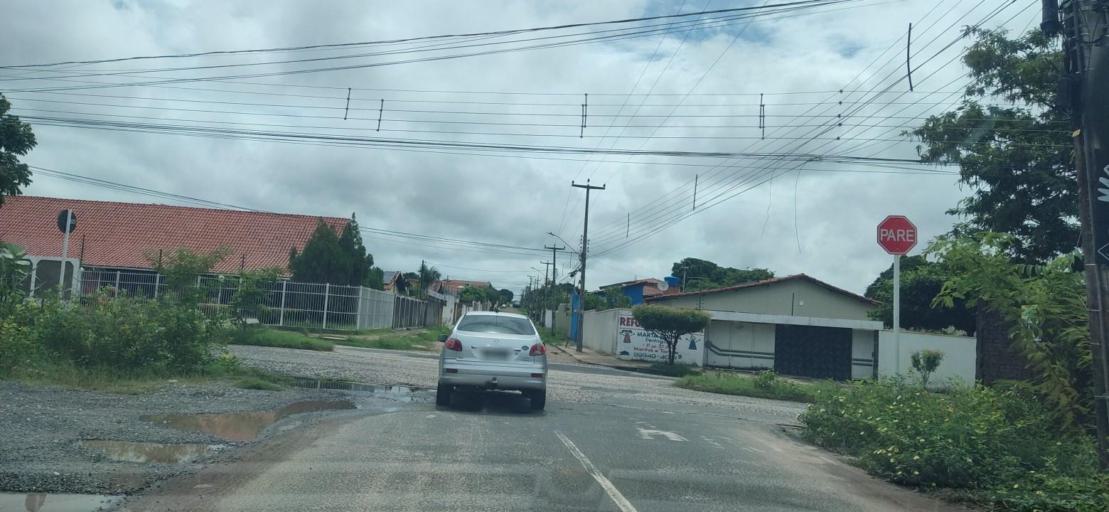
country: BR
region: Piaui
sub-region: Teresina
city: Teresina
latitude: -5.0723
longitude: -42.7693
